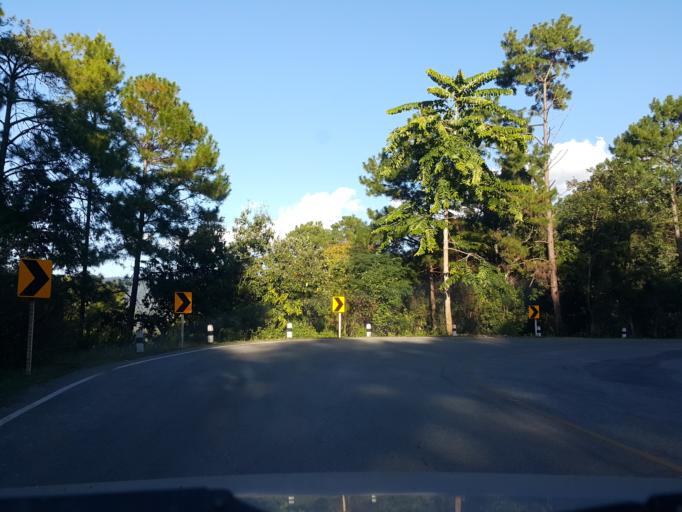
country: TH
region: Mae Hong Son
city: Mae Hi
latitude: 19.2731
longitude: 98.5501
